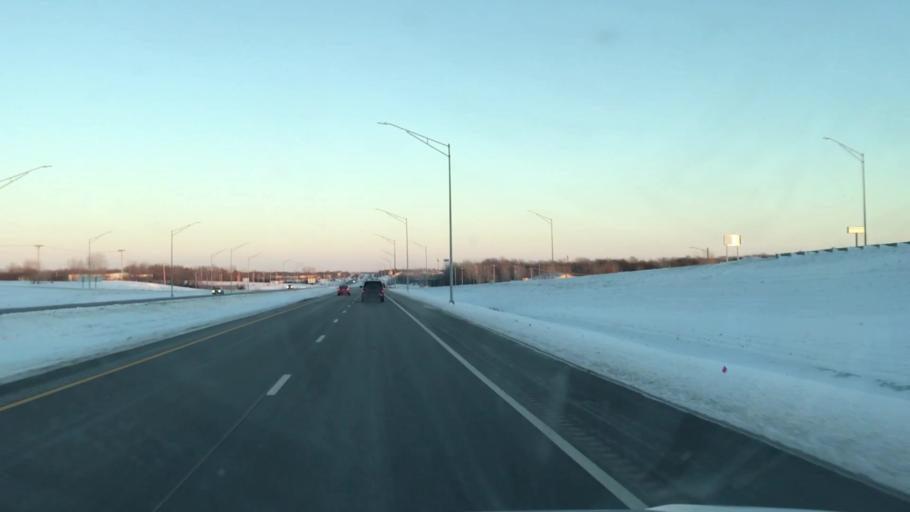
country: US
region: Missouri
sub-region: Clinton County
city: Cameron
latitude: 39.7543
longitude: -94.2337
